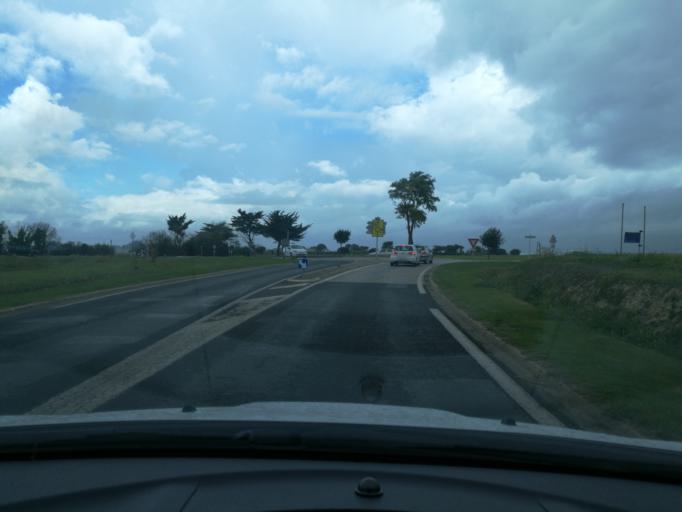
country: FR
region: Poitou-Charentes
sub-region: Departement de la Charente-Maritime
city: Saint-Martin-de-Re
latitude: 46.2006
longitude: -1.3742
